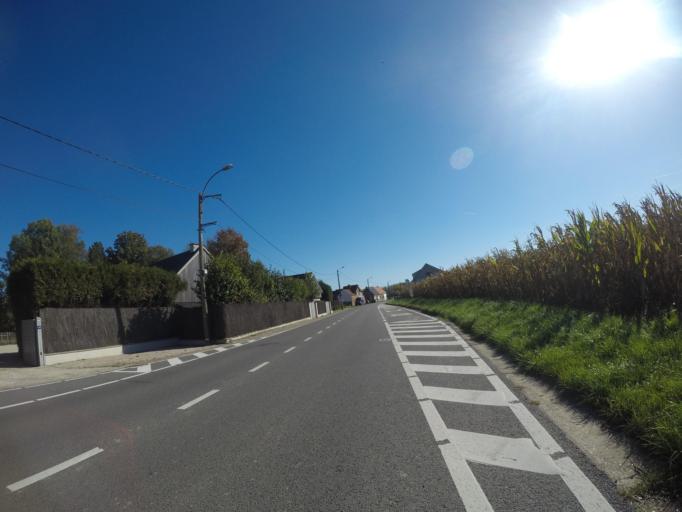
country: BE
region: Flanders
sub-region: Provincie Limburg
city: Alken
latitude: 50.8615
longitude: 5.3144
